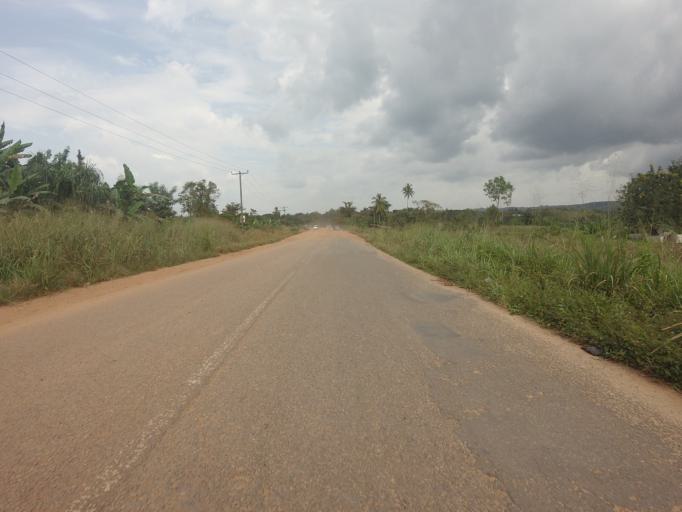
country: GH
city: Akropong
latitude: 5.9571
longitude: -0.1539
